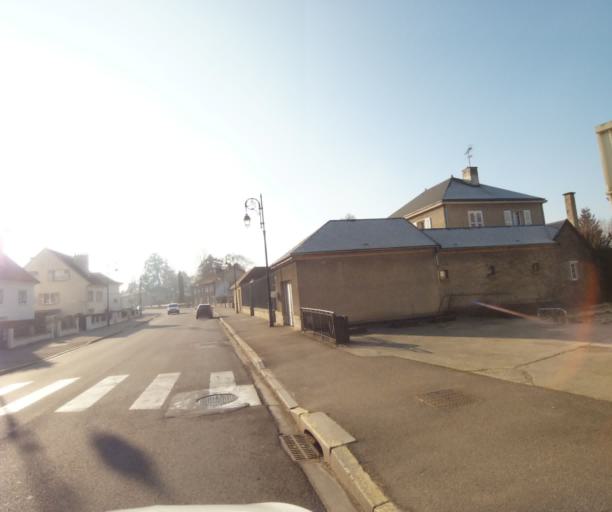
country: FR
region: Champagne-Ardenne
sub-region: Departement de la Haute-Marne
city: Montier-en-Der
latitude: 48.4793
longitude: 4.7686
